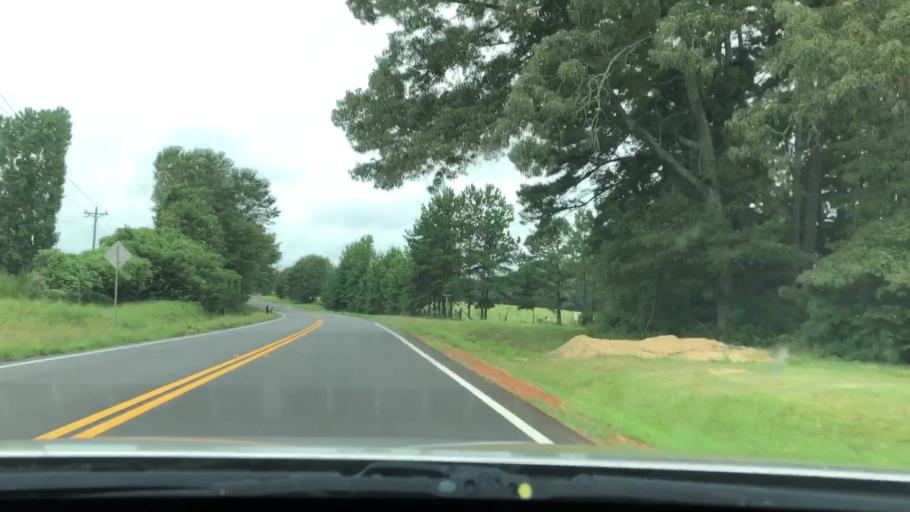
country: US
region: Georgia
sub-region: Upson County
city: Hannahs Mill
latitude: 33.0128
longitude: -84.4363
